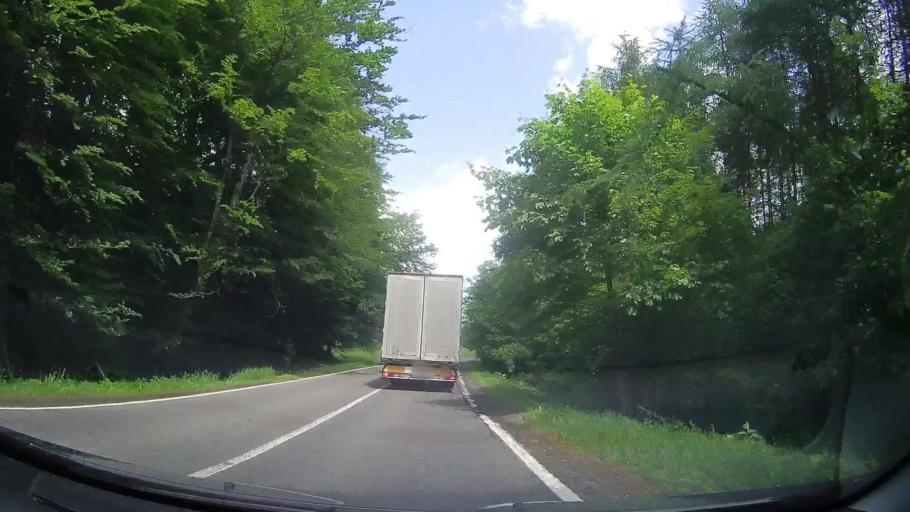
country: RO
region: Prahova
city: Maneciu
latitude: 45.4128
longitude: 25.9424
